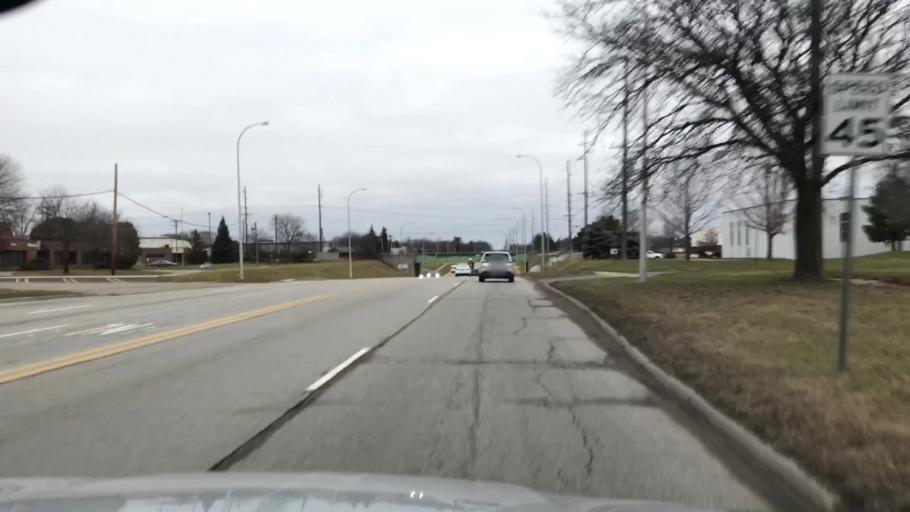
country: US
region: Michigan
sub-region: Wayne County
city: Westland
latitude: 42.3751
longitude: -83.4116
